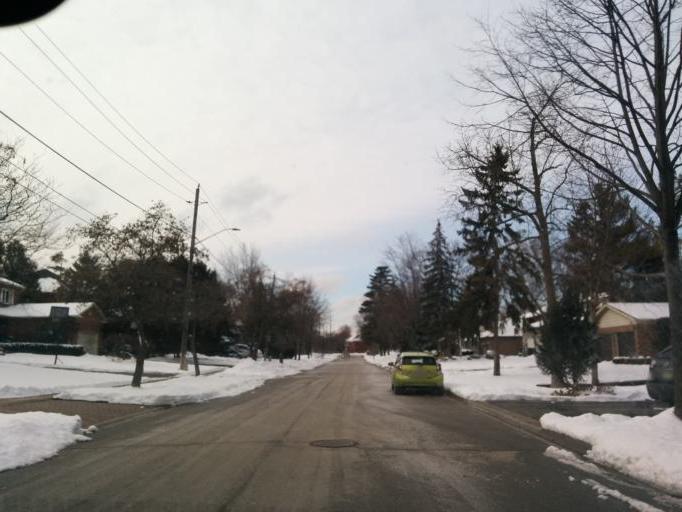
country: CA
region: Ontario
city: Mississauga
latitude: 43.5366
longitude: -79.6617
